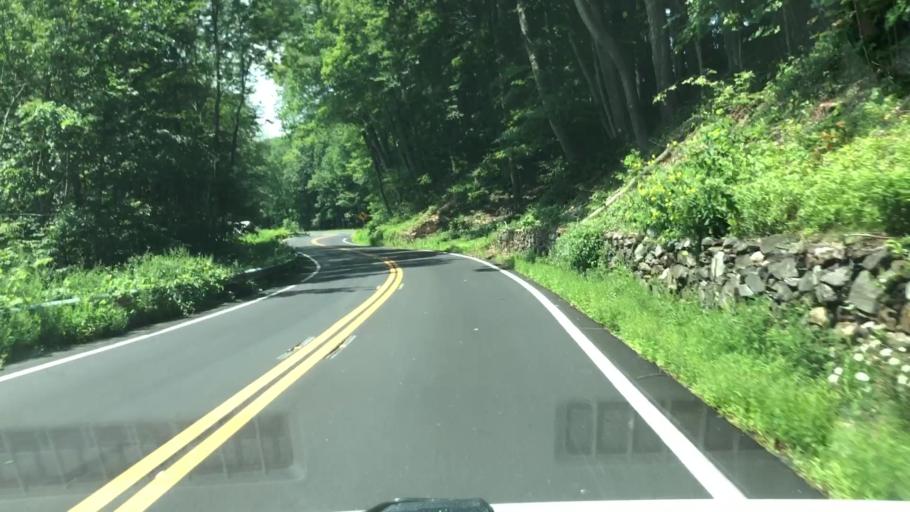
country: US
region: Massachusetts
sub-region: Franklin County
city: Ashfield
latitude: 42.5093
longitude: -72.7604
